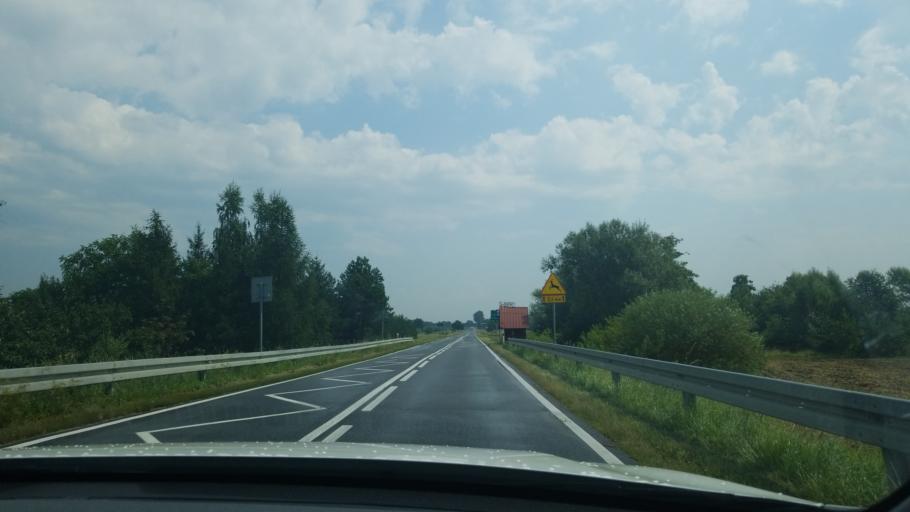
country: PL
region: Lesser Poland Voivodeship
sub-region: Powiat bochenski
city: Dziewin
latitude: 50.1257
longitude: 20.4568
